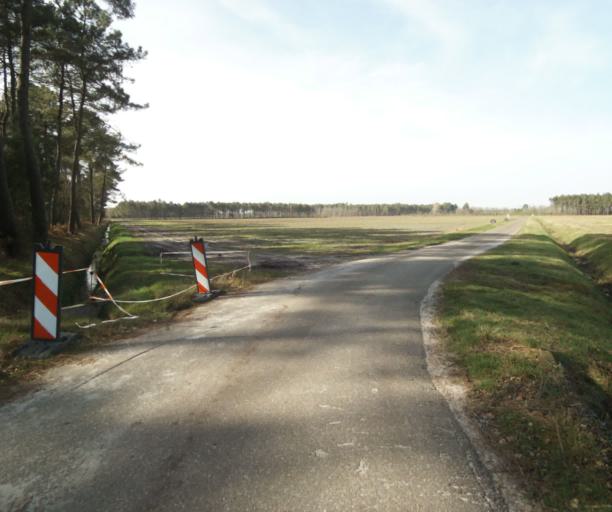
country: FR
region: Aquitaine
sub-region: Departement des Landes
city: Roquefort
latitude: 44.1415
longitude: -0.1591
